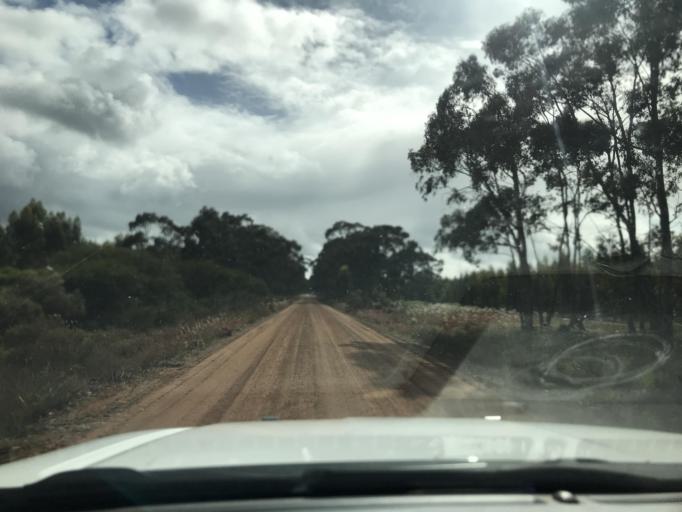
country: AU
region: South Australia
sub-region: Wattle Range
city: Penola
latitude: -37.1873
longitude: 141.1938
